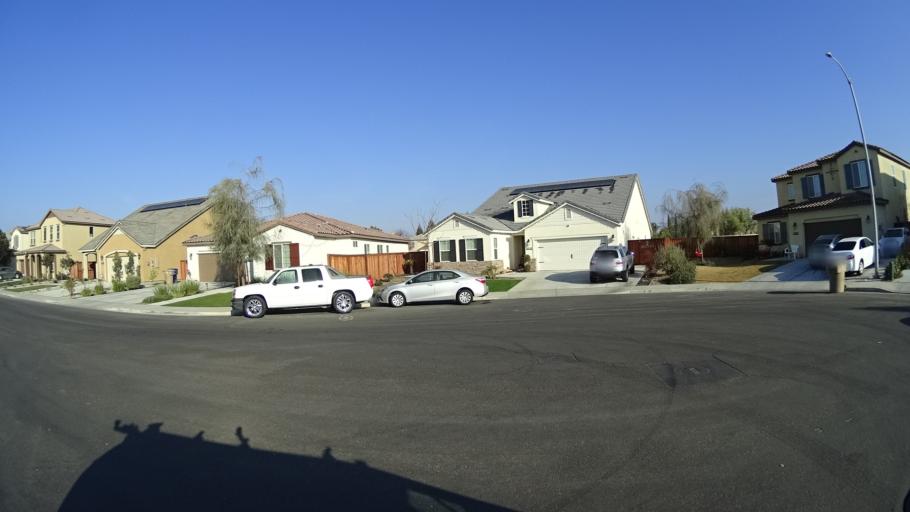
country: US
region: California
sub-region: Kern County
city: Greenacres
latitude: 35.3027
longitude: -119.1150
